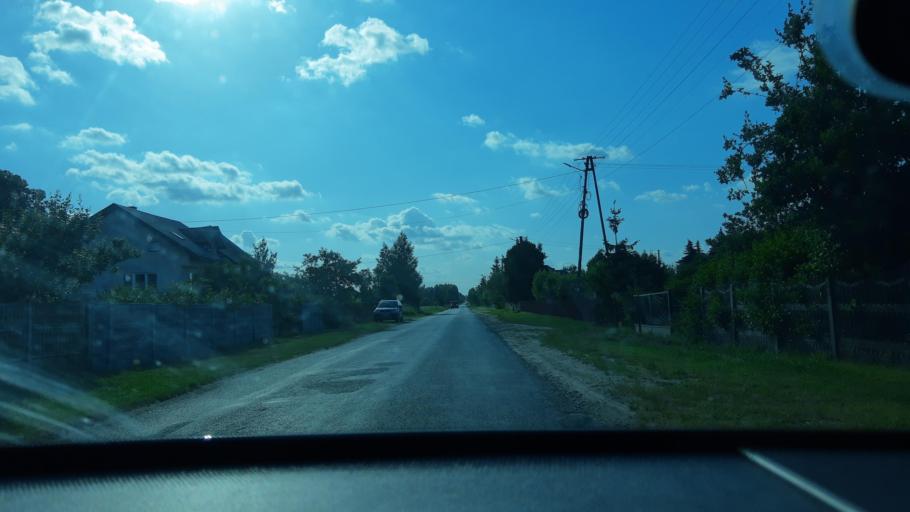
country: PL
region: Lodz Voivodeship
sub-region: Powiat zdunskowolski
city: Zapolice
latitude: 51.5392
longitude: 18.8050
